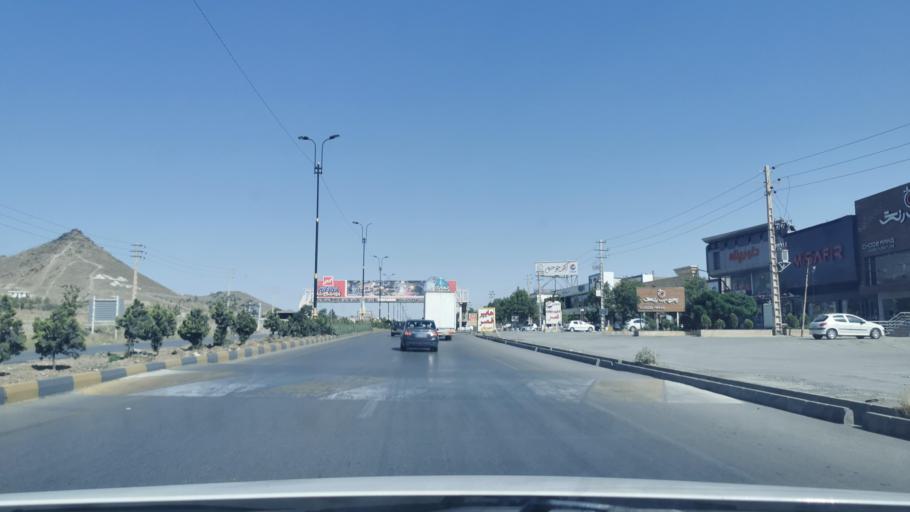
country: IR
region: Razavi Khorasan
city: Torqabeh
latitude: 36.3924
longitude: 59.4024
